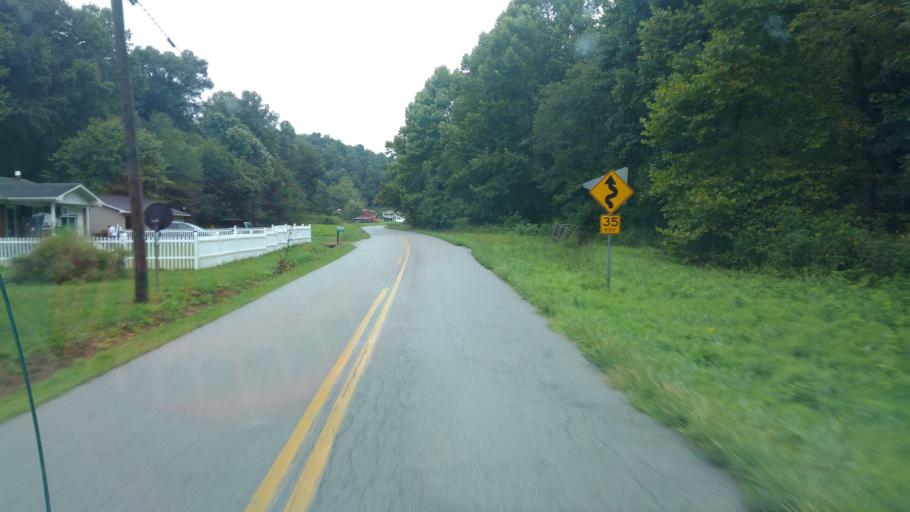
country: US
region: Kentucky
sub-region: Fleming County
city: Flemingsburg
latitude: 38.4227
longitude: -83.5218
